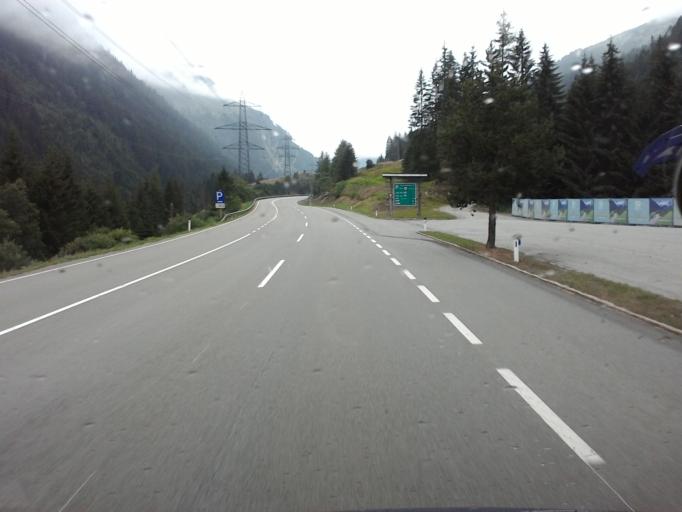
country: AT
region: Tyrol
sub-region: Politischer Bezirk Lienz
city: Matrei in Osttirol
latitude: 47.0917
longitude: 12.5228
